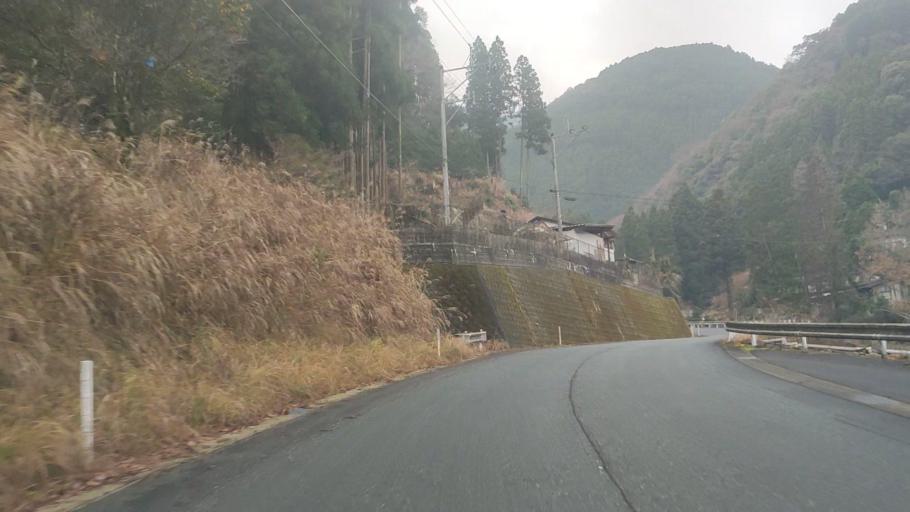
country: JP
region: Kumamoto
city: Matsubase
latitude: 32.5972
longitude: 130.8890
